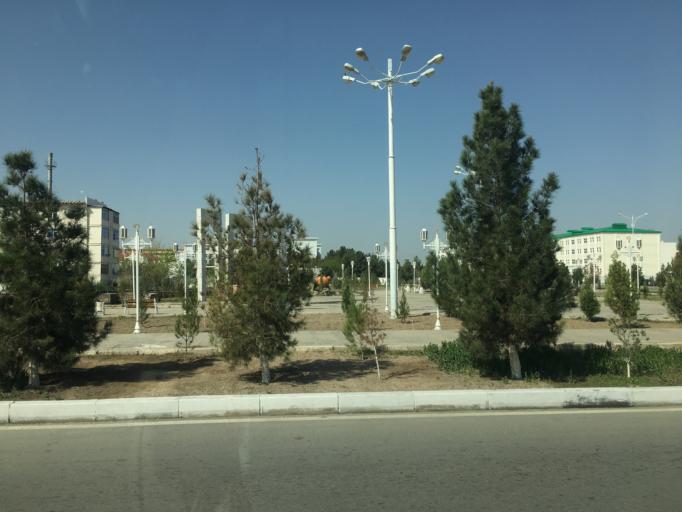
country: TM
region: Lebap
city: Turkmenabat
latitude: 39.0413
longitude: 63.5884
